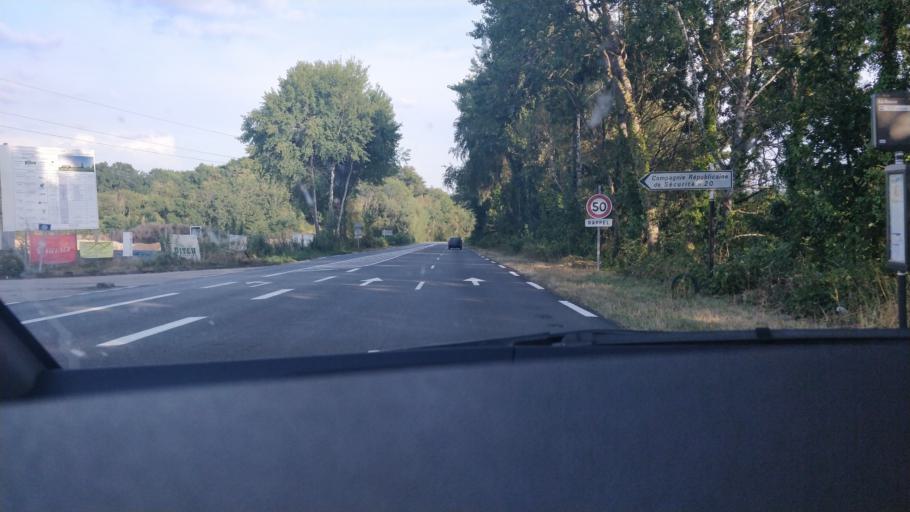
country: FR
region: Limousin
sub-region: Departement de la Haute-Vienne
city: Le Palais-sur-Vienne
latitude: 45.8562
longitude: 1.2917
